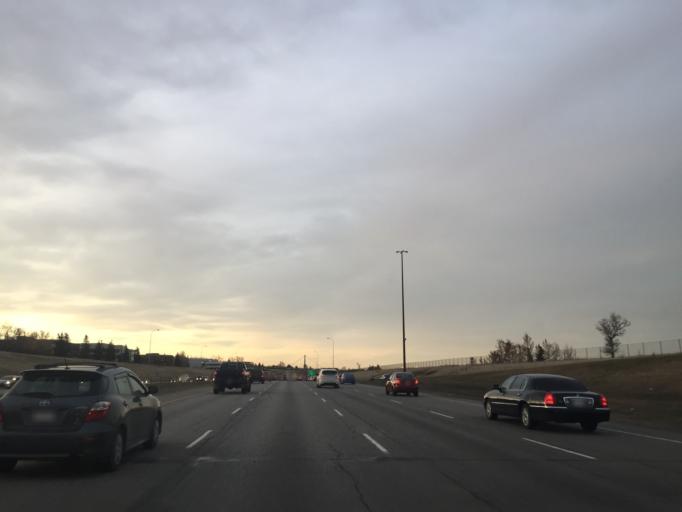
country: CA
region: Alberta
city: Calgary
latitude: 51.0804
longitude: -114.0330
